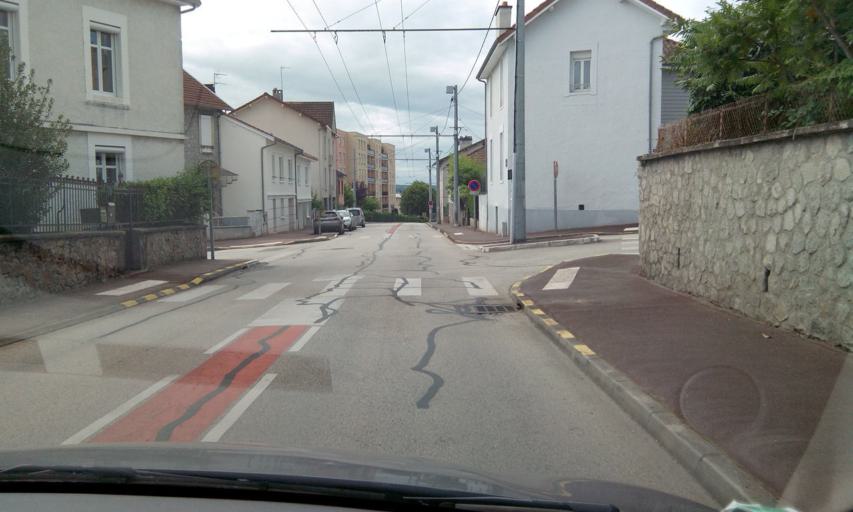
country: FR
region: Limousin
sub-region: Departement de la Haute-Vienne
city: Limoges
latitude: 45.8475
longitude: 1.2717
